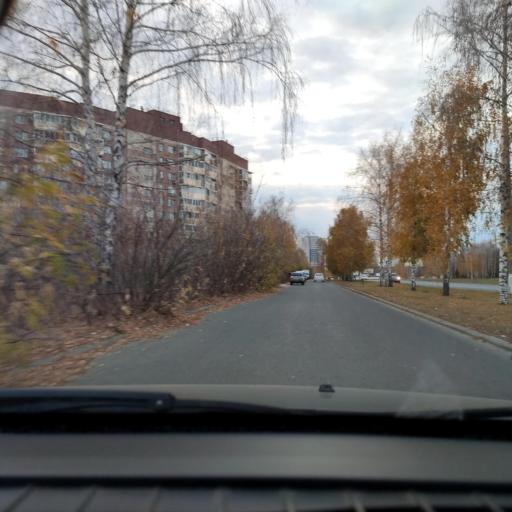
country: RU
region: Samara
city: Tol'yatti
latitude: 53.5021
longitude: 49.2615
